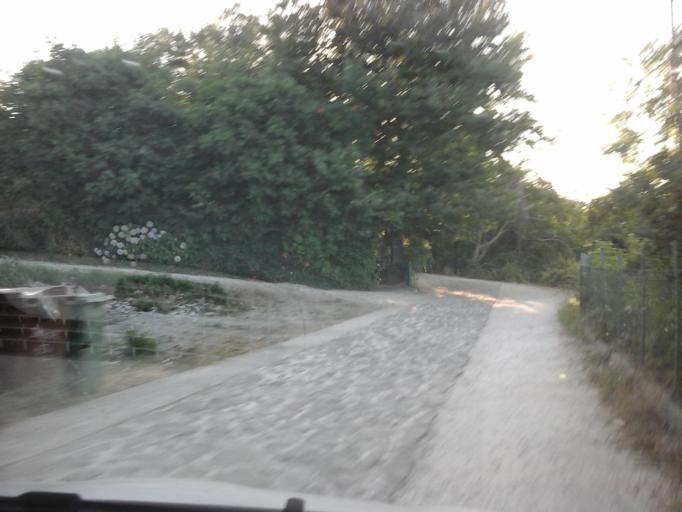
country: GR
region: East Macedonia and Thrace
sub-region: Nomos Evrou
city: Samothraki
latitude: 40.4948
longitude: 25.6106
